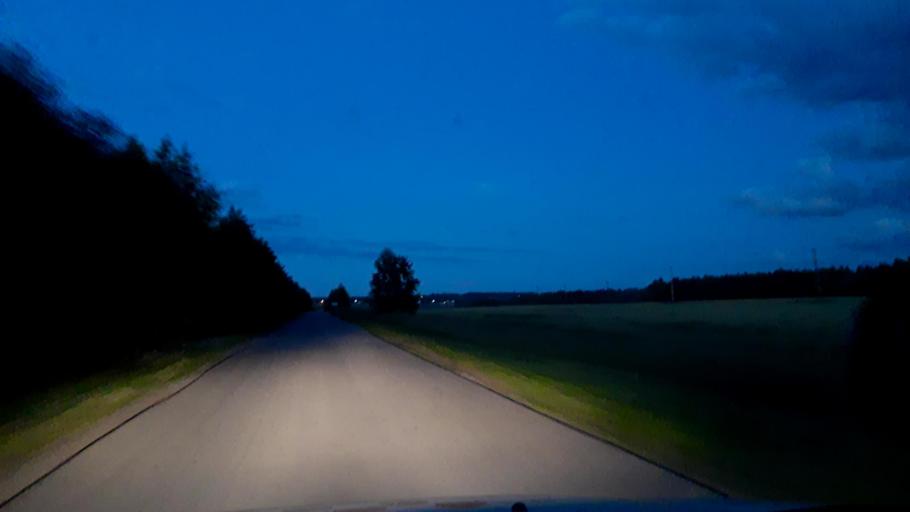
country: RU
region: Nizjnij Novgorod
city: Pamyat' Parizhskoy Kommuny
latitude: 56.0592
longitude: 44.4806
